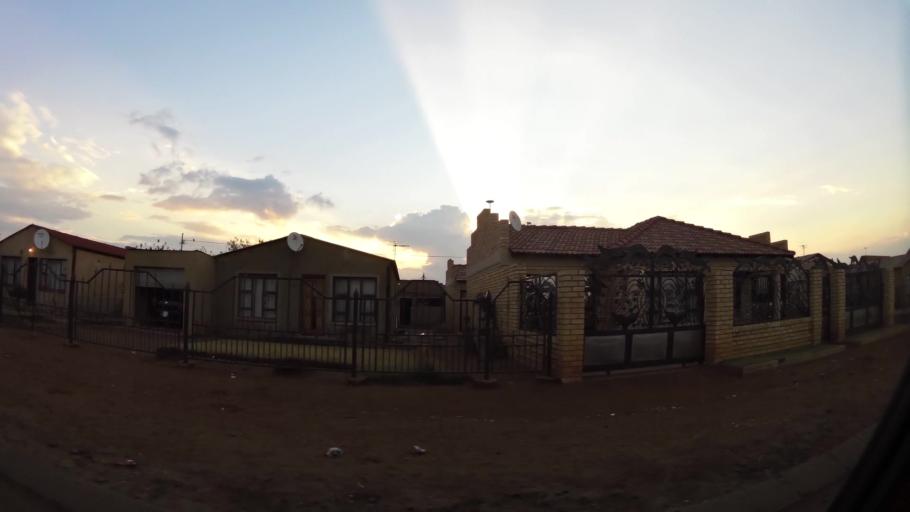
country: ZA
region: Gauteng
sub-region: City of Johannesburg Metropolitan Municipality
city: Orange Farm
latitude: -26.5517
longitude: 27.8638
